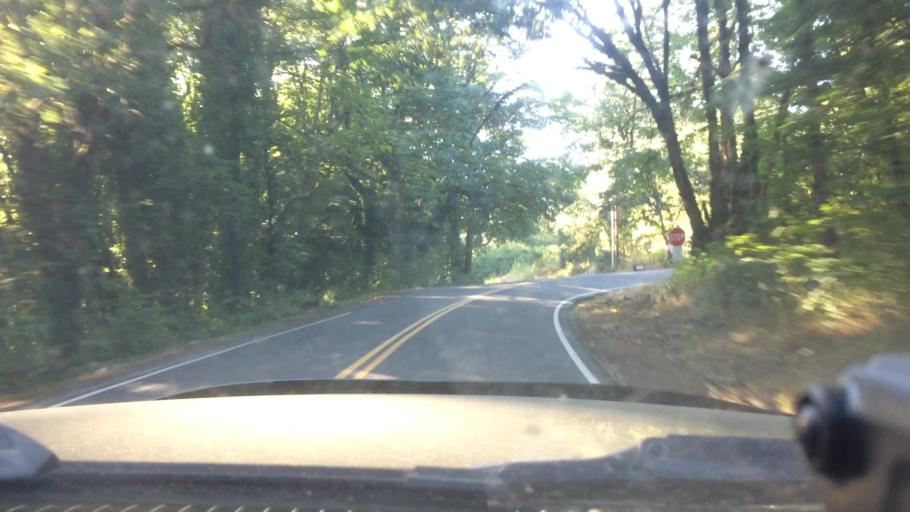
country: US
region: Oregon
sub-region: Yamhill County
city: Newberg
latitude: 45.3312
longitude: -122.9305
